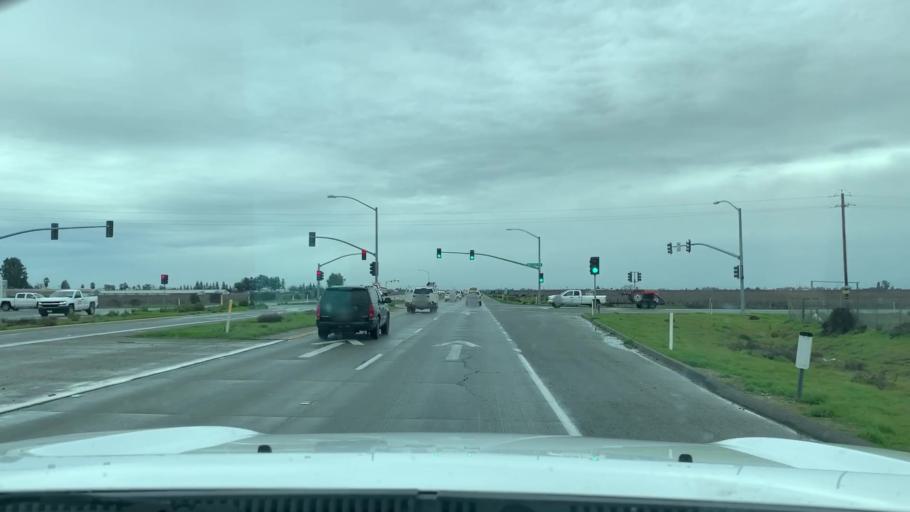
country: US
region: California
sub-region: Fresno County
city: Caruthers
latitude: 36.5467
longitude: -119.7860
